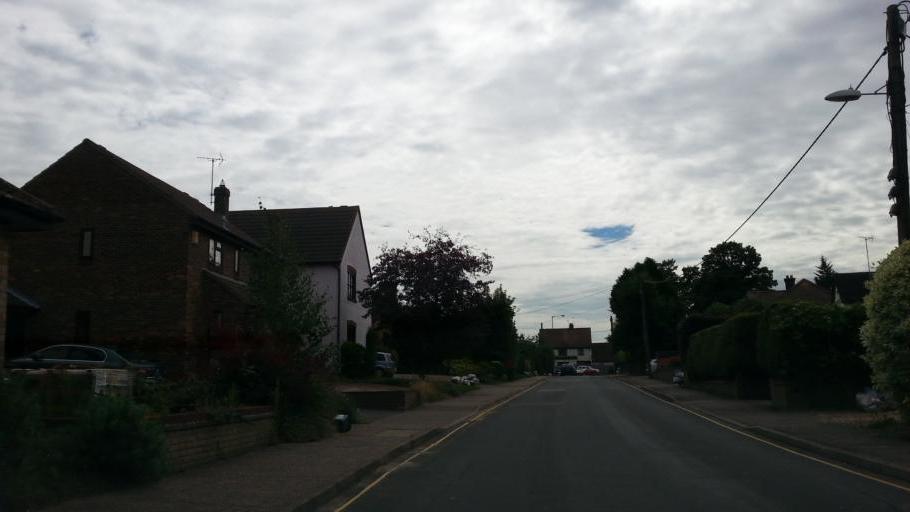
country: GB
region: England
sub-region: Essex
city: Kelvedon
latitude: 51.8450
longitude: 0.7144
